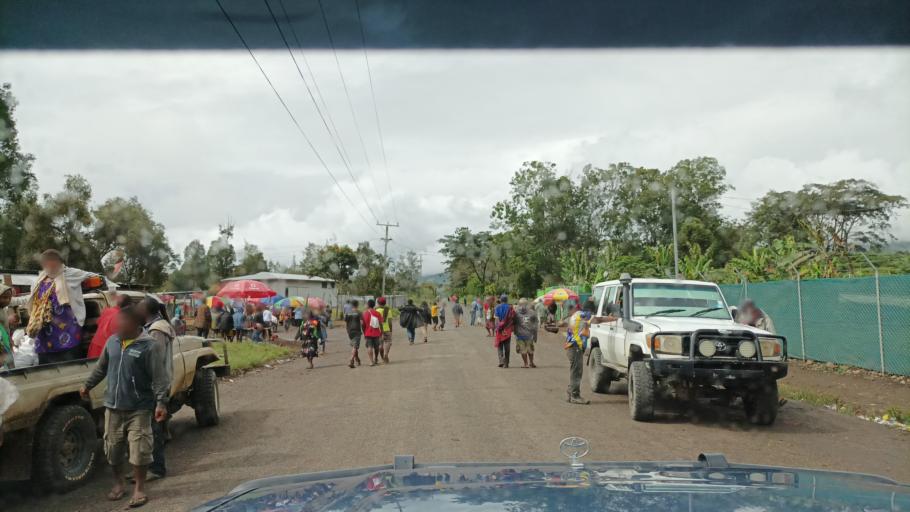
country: PG
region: Jiwaka
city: Minj
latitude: -5.8815
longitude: 144.6805
